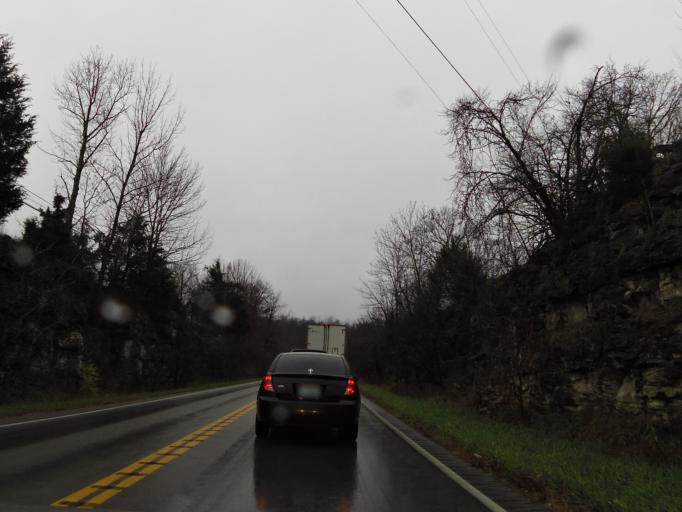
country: US
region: Kentucky
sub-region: Rockcastle County
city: Mount Vernon
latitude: 37.4171
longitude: -84.3335
